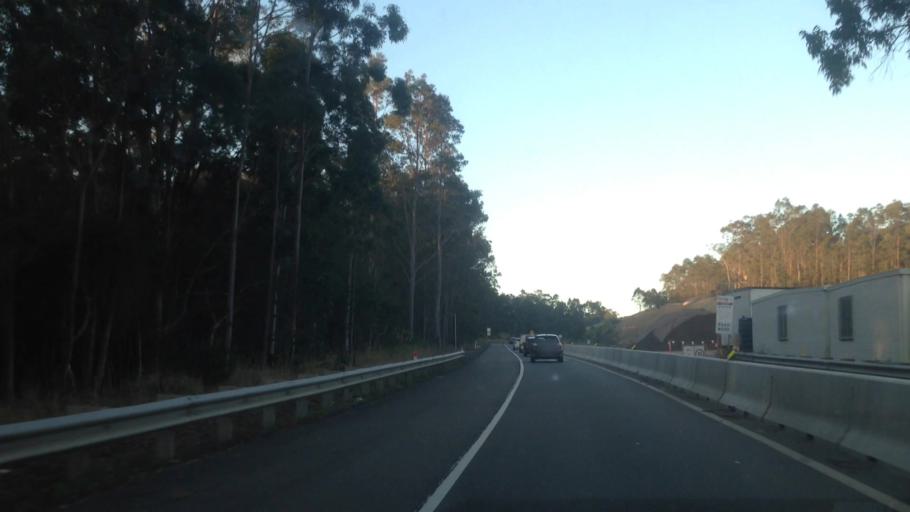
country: AU
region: New South Wales
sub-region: Wyong Shire
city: Jilliby
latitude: -33.2187
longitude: 151.4395
